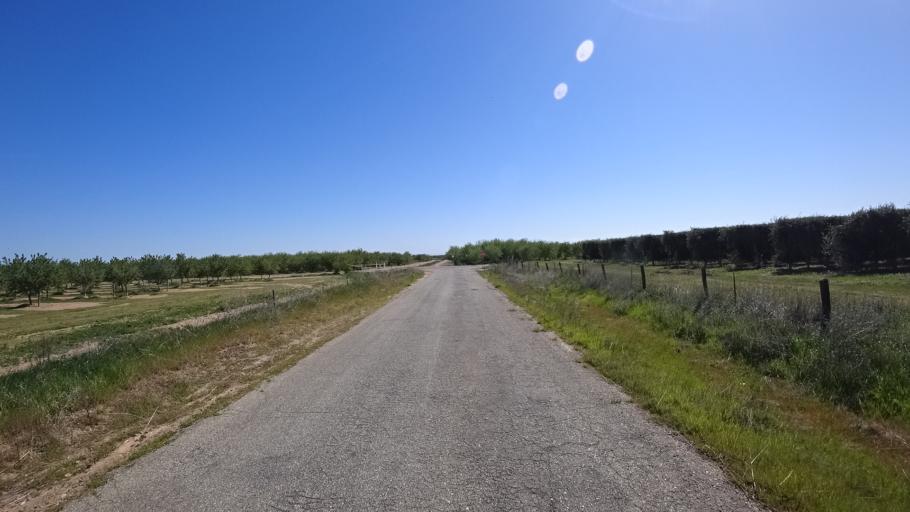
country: US
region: California
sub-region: Glenn County
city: Orland
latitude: 39.6538
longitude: -122.2541
